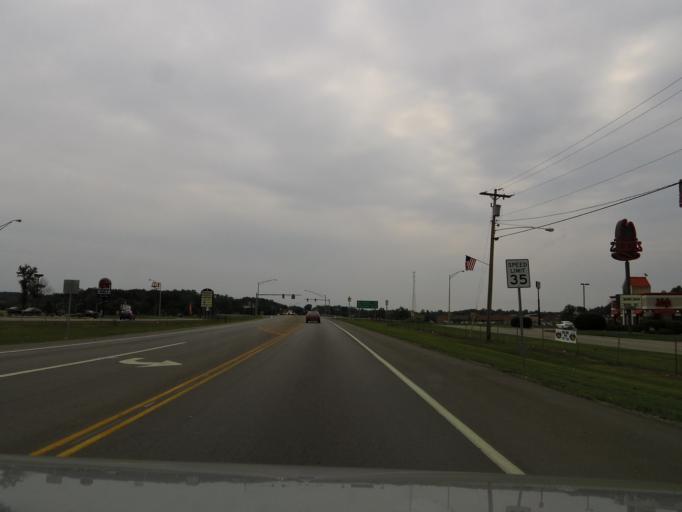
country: US
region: Ohio
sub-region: Brown County
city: Mount Orab
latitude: 39.0444
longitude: -83.9218
